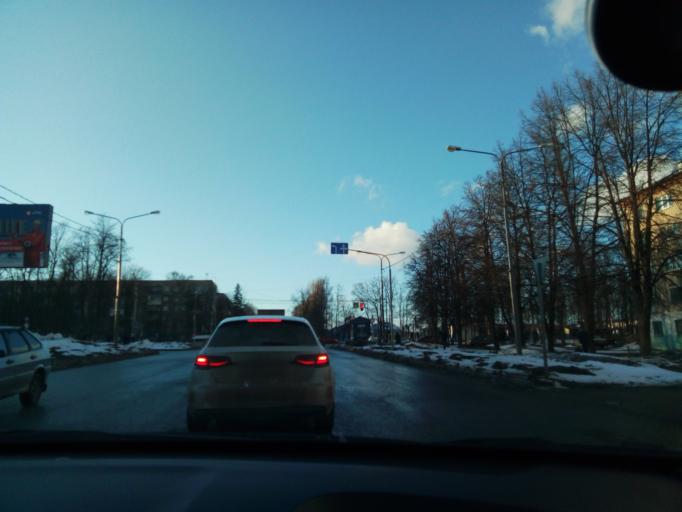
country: RU
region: Chuvashia
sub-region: Cheboksarskiy Rayon
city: Cheboksary
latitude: 56.1402
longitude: 47.1990
